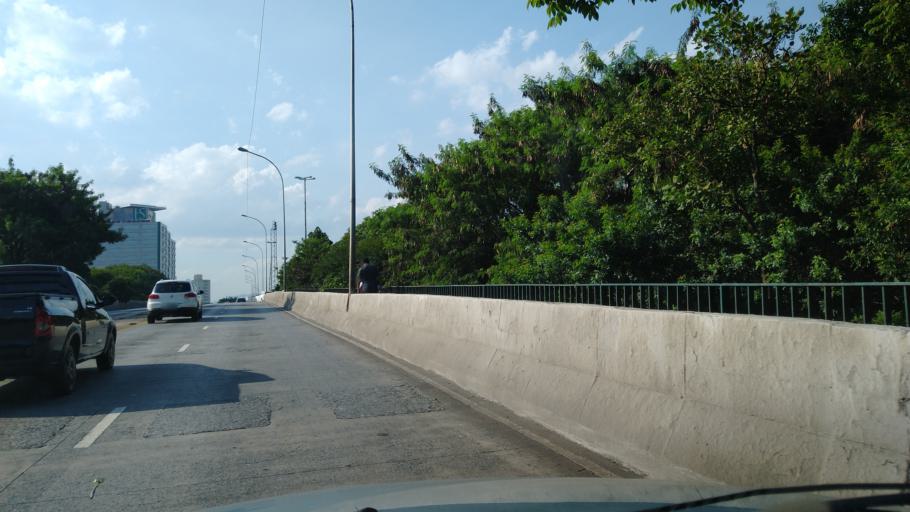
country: BR
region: Sao Paulo
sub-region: Sao Paulo
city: Sao Paulo
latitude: -23.5495
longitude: -46.6016
